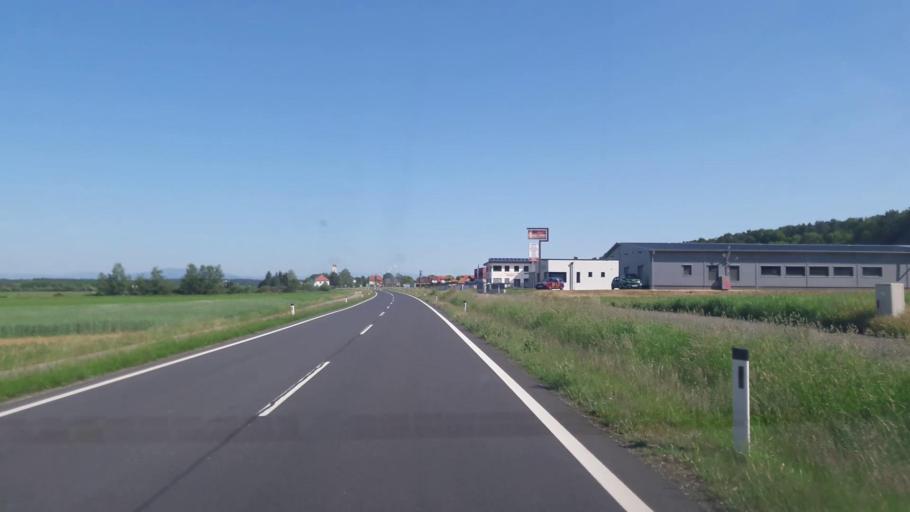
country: AT
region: Burgenland
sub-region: Politischer Bezirk Jennersdorf
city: Deutsch Kaltenbrunn
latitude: 47.0762
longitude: 16.1117
